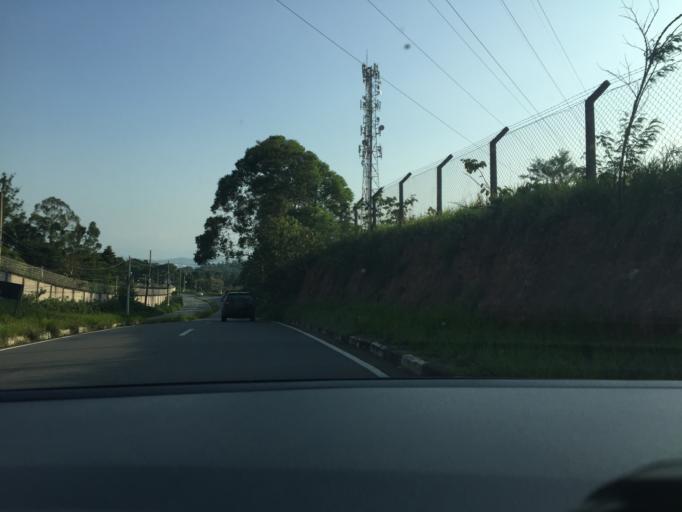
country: BR
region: Sao Paulo
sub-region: Vinhedo
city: Vinhedo
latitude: -23.0188
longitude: -47.0012
